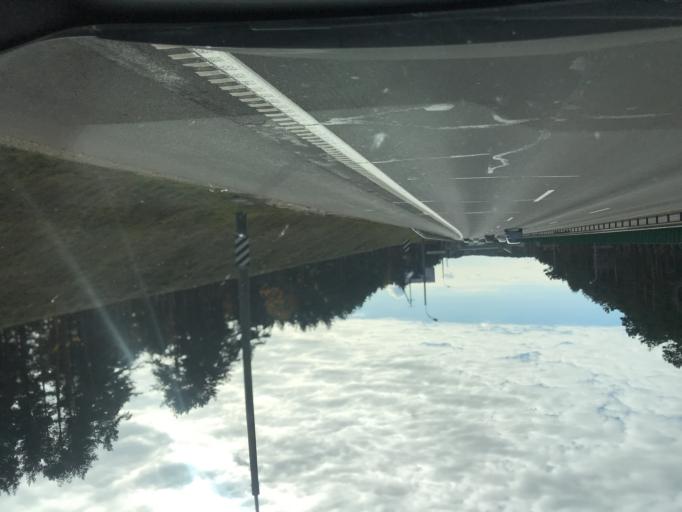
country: BY
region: Minsk
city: Vyaliki Trastsyanets
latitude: 53.8962
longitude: 27.6914
